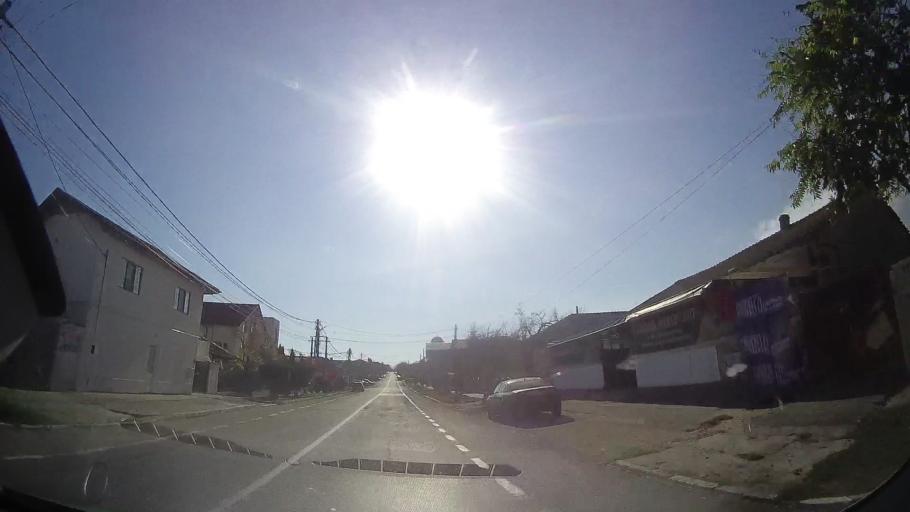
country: RO
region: Constanta
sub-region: Comuna Costinesti
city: Schitu
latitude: 43.9444
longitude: 28.6297
